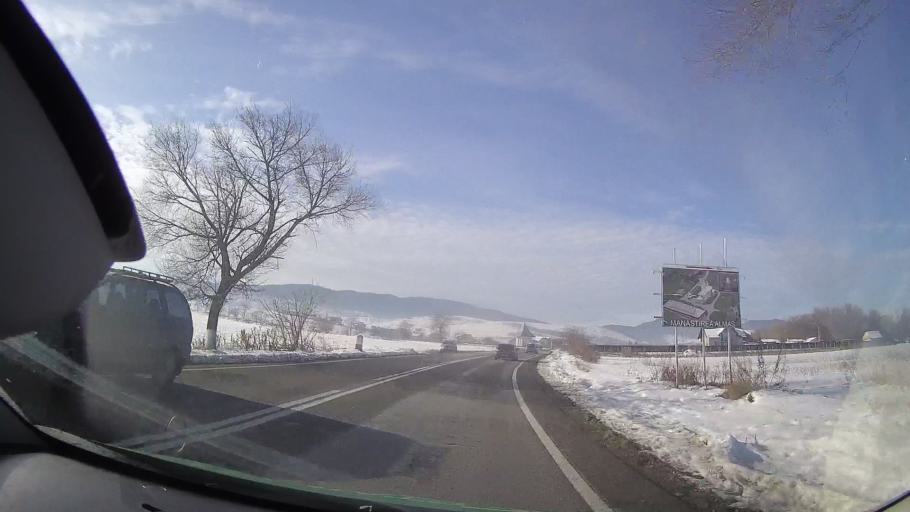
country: RO
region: Neamt
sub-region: Comuna Negresti
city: Negresti
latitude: 46.9978
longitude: 26.3710
